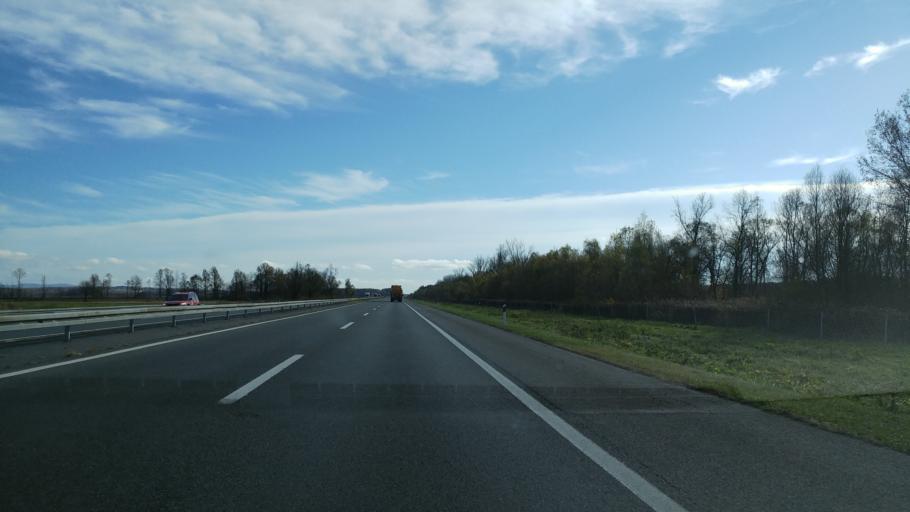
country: HR
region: Sisacko-Moslavacka
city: Husain
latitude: 45.4282
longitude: 16.8366
